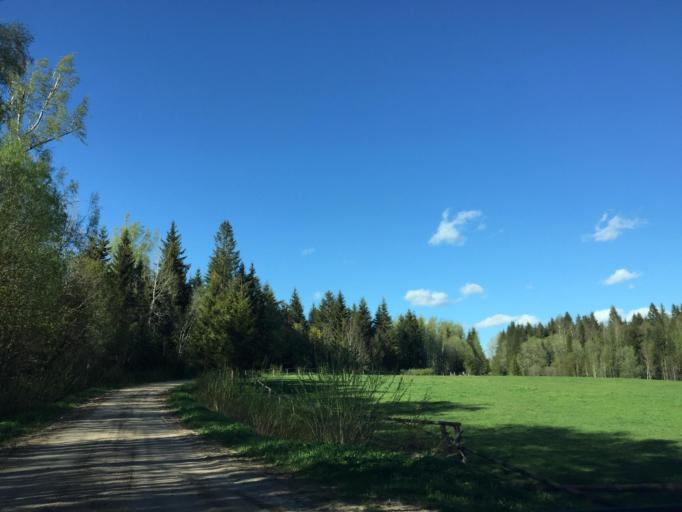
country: LV
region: Vecpiebalga
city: Vecpiebalga
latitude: 56.8560
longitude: 25.9580
